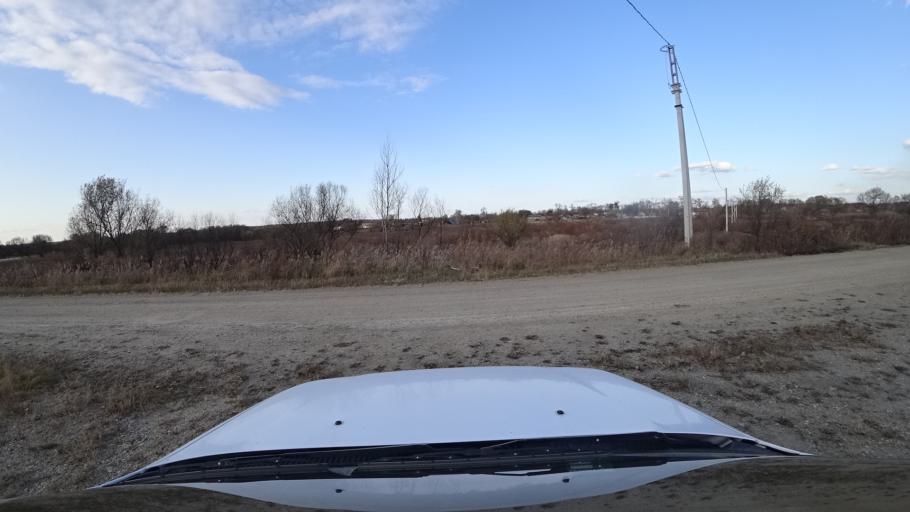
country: RU
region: Primorskiy
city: Lazo
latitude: 45.8247
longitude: 133.6108
